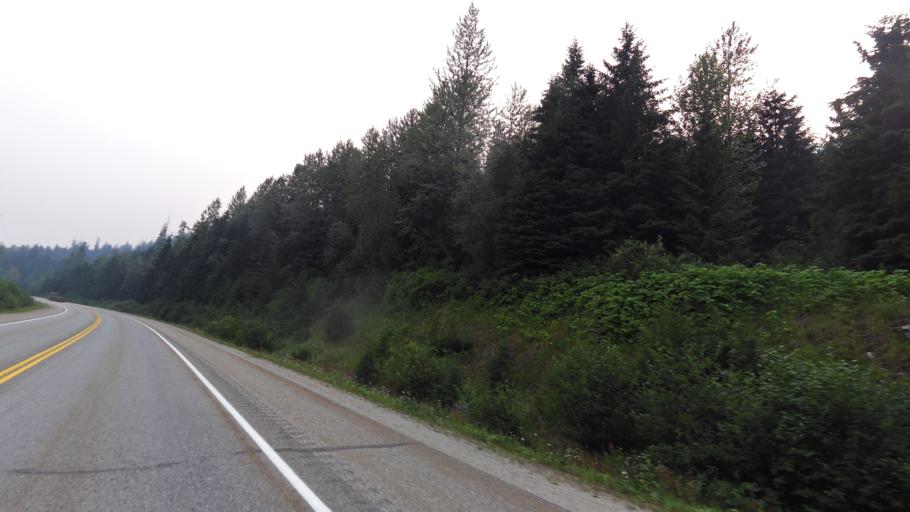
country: CA
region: Alberta
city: Jasper Park Lodge
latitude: 52.3243
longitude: -119.1785
